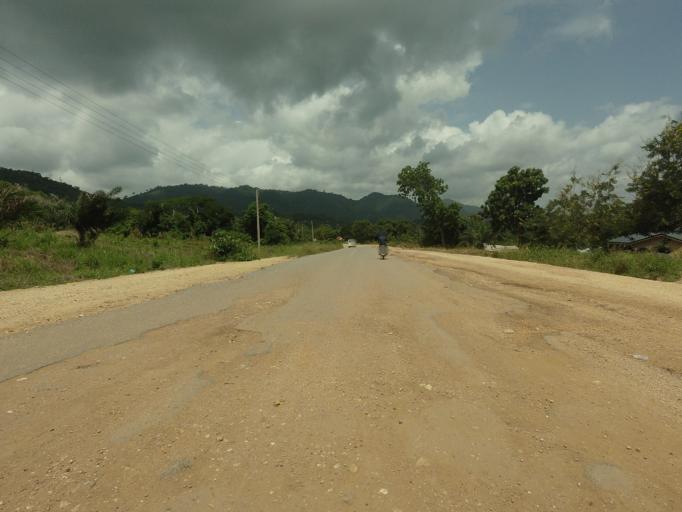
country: GH
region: Volta
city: Ho
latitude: 6.6981
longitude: 0.3352
